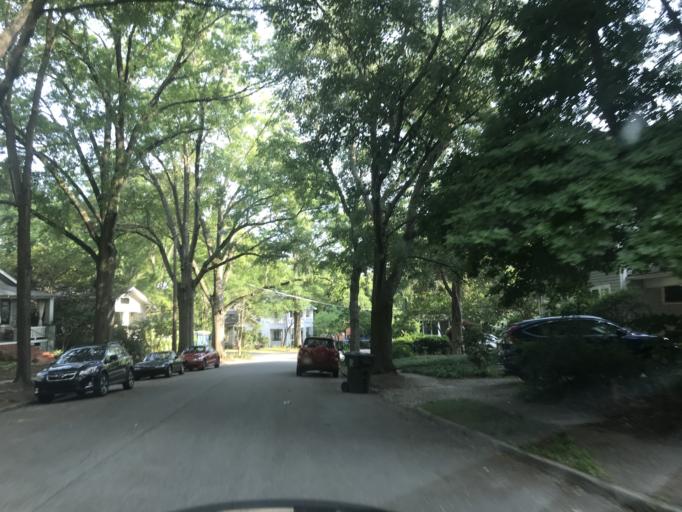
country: US
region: North Carolina
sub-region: Wake County
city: Raleigh
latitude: 35.7741
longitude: -78.6519
